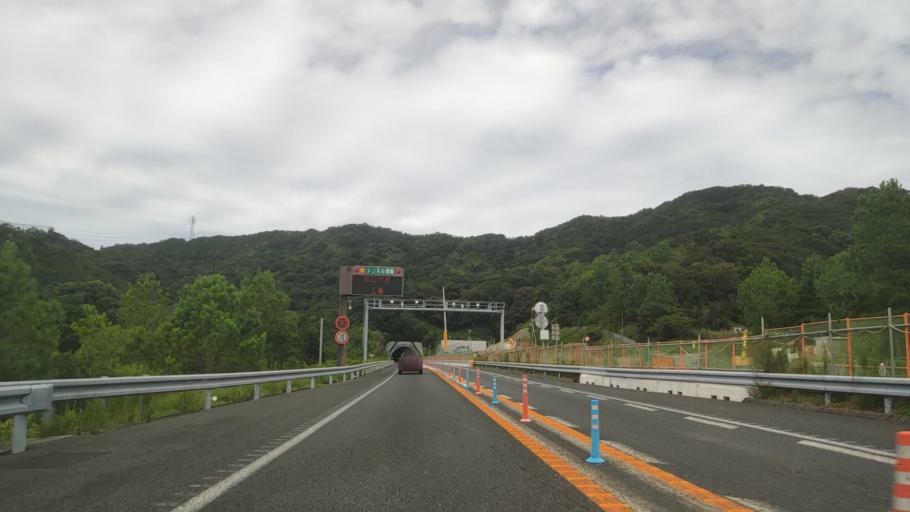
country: JP
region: Wakayama
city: Gobo
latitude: 33.8468
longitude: 135.2177
